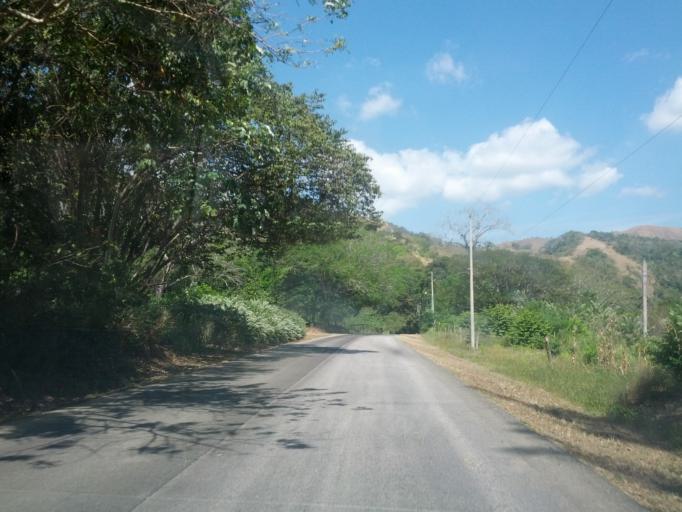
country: CR
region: Puntarenas
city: Buenos Aires
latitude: 8.9639
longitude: -83.3079
